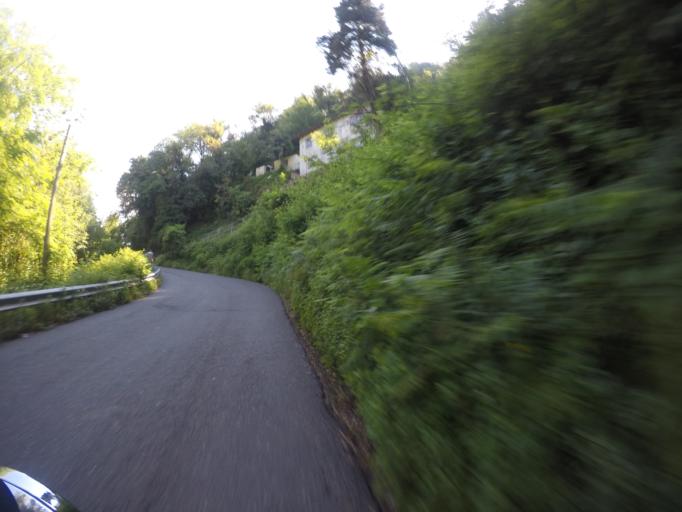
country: IT
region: Tuscany
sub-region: Provincia di Massa-Carrara
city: Montignoso
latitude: 44.0498
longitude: 10.1608
